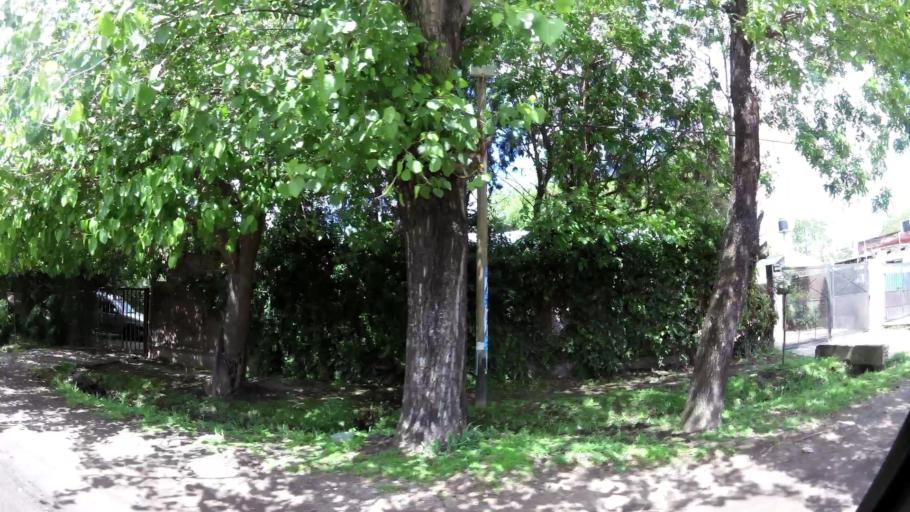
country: AR
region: Buenos Aires
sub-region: Partido de Quilmes
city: Quilmes
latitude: -34.8281
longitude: -58.2143
